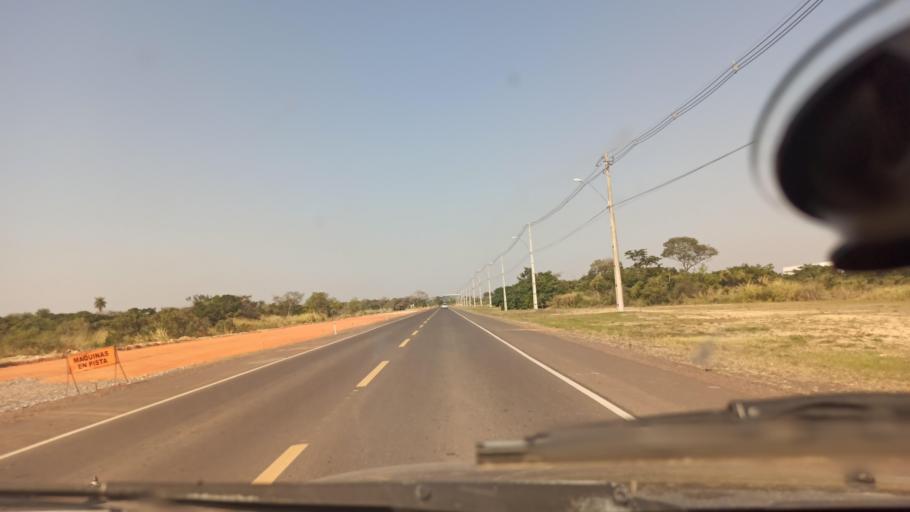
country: PY
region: Central
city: Colonia Mariano Roque Alonso
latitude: -25.1913
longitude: -57.5777
